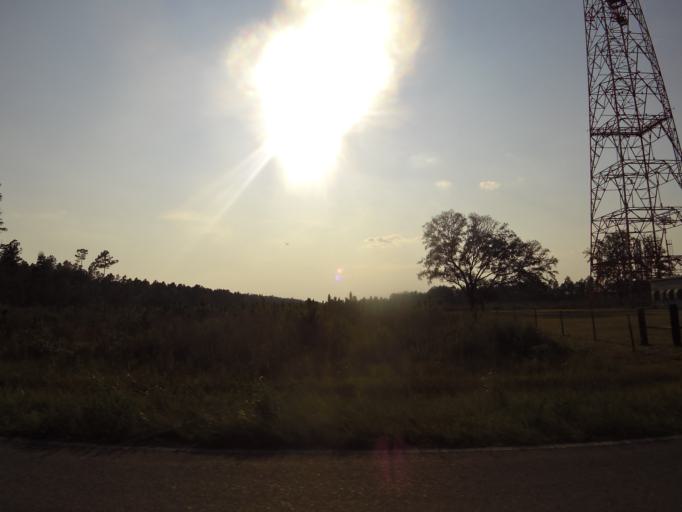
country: US
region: Florida
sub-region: Duval County
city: Baldwin
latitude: 30.3403
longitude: -82.0090
